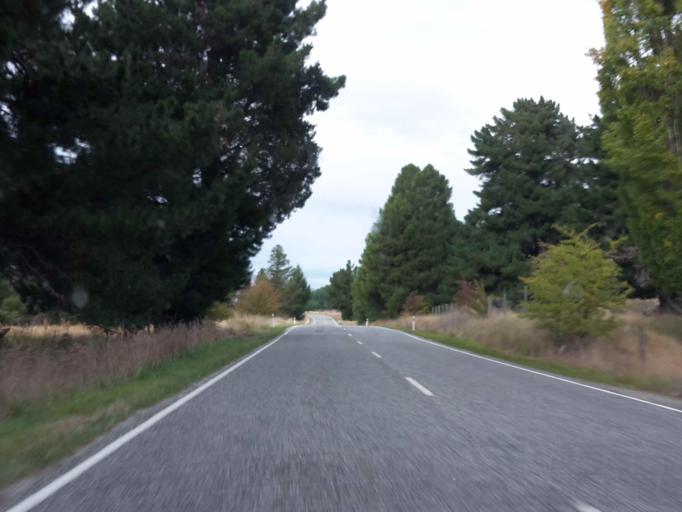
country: NZ
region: Otago
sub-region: Queenstown-Lakes District
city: Wanaka
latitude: -44.7638
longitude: 169.0970
